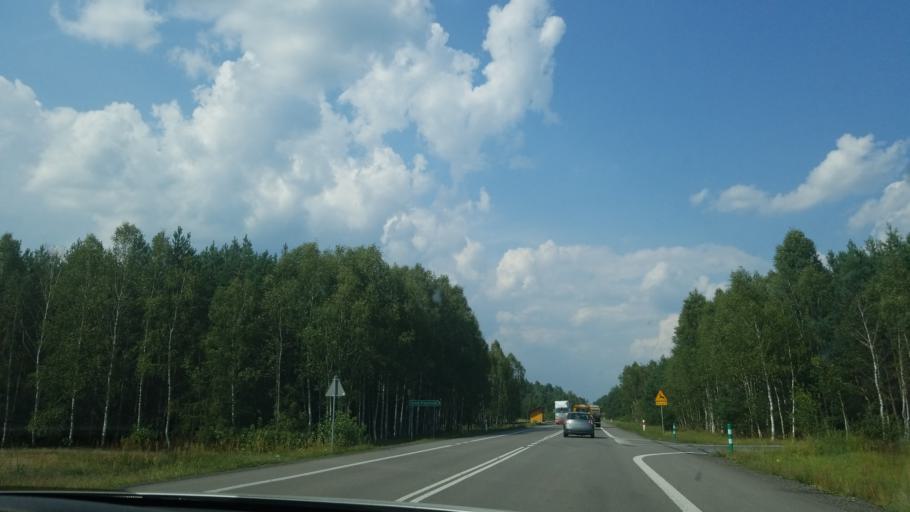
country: PL
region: Subcarpathian Voivodeship
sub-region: Powiat nizanski
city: Jarocin
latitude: 50.6242
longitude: 22.2866
